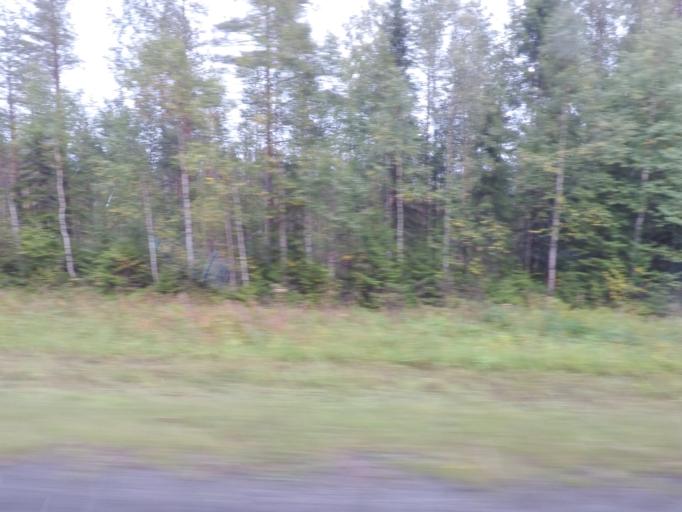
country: FI
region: Southern Savonia
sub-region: Pieksaemaeki
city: Joroinen
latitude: 62.0389
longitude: 27.8003
